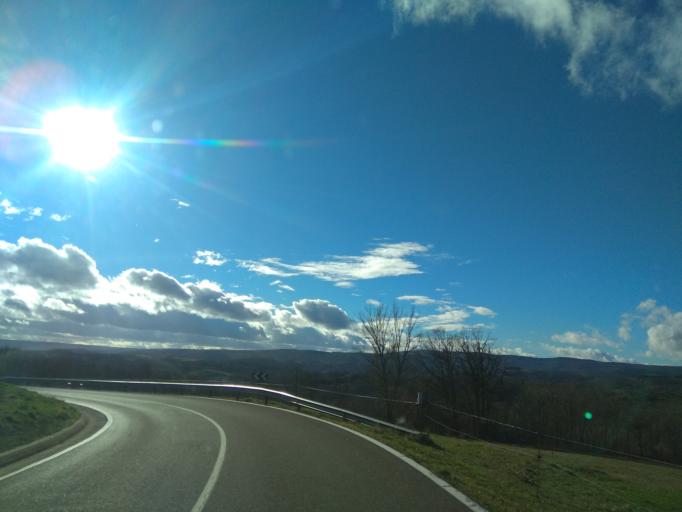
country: ES
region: Cantabria
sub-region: Provincia de Cantabria
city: San Martin de Elines
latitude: 42.9157
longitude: -3.8674
